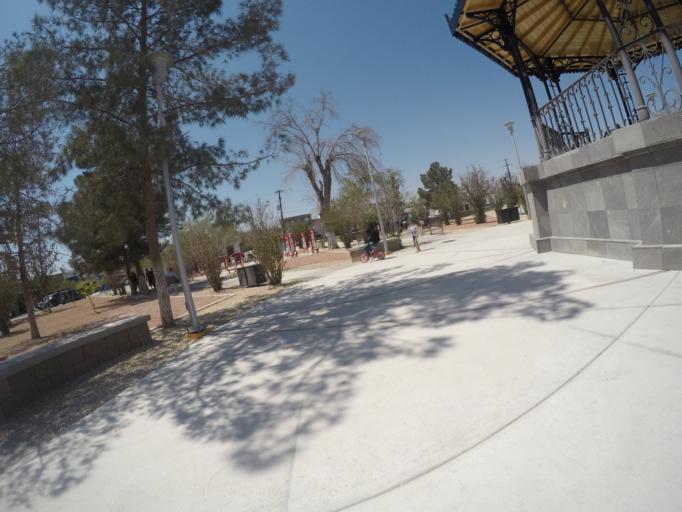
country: MX
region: Chihuahua
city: Ciudad Juarez
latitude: 31.7304
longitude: -106.4821
